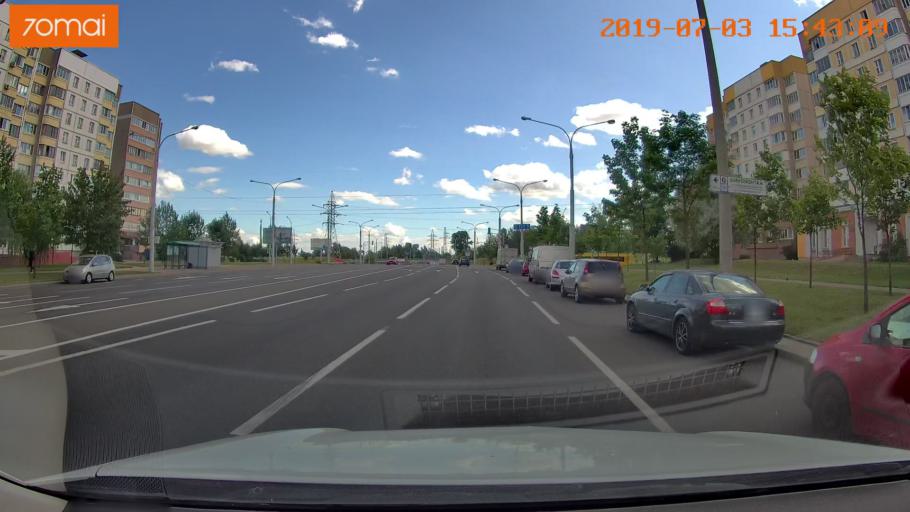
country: BY
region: Minsk
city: Syenitsa
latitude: 53.8366
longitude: 27.5744
